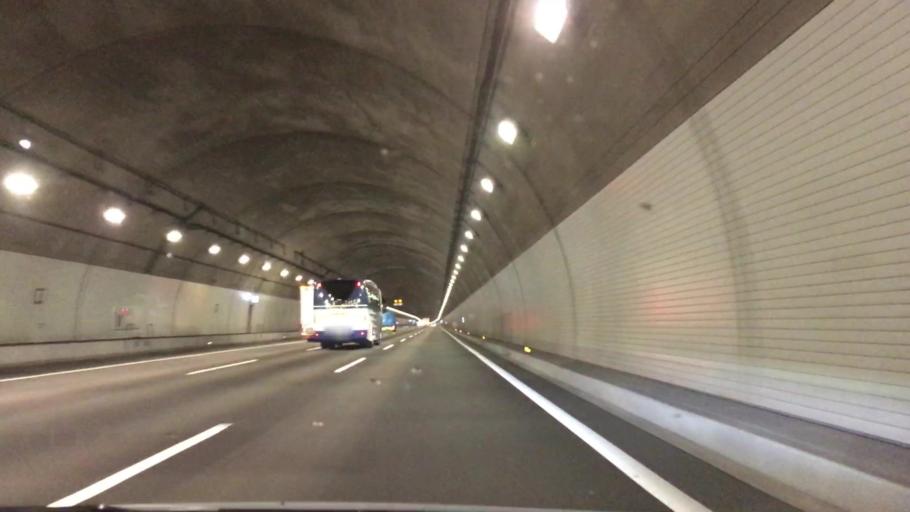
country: JP
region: Shizuoka
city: Fujieda
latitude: 34.9580
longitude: 138.2868
